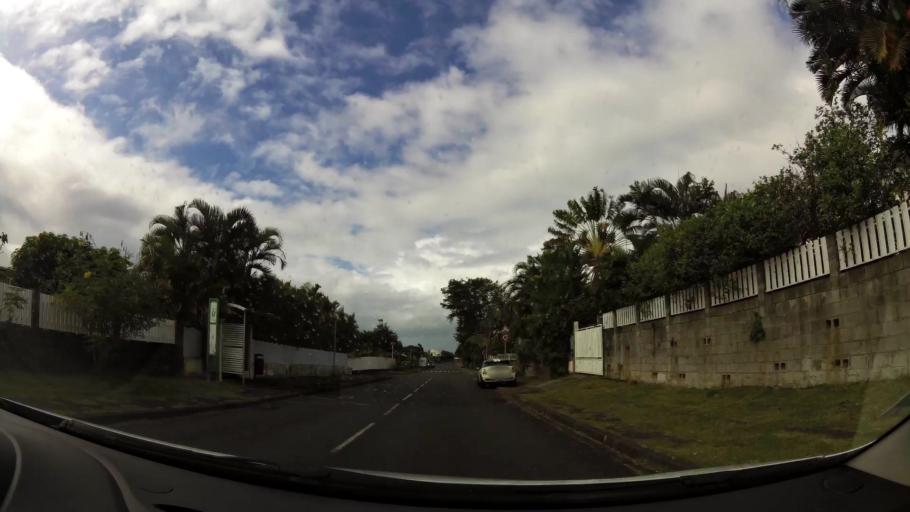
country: RE
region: Reunion
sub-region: Reunion
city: Sainte-Marie
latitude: -20.8957
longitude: 55.5692
